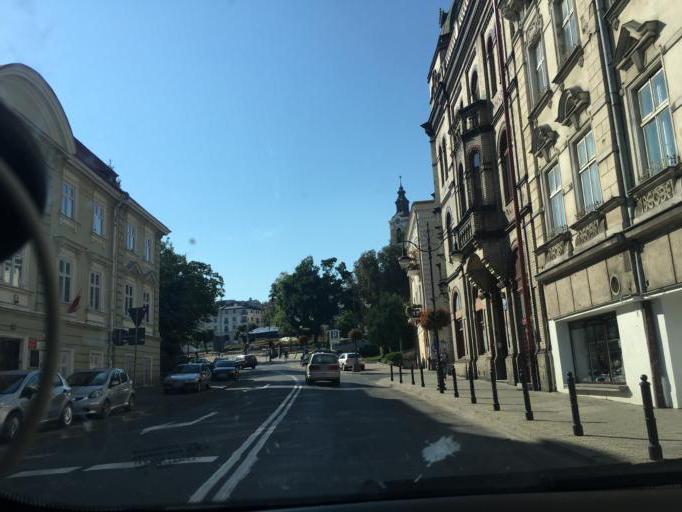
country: PL
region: Subcarpathian Voivodeship
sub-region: Przemysl
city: Przemysl
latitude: 49.7837
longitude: 22.7678
